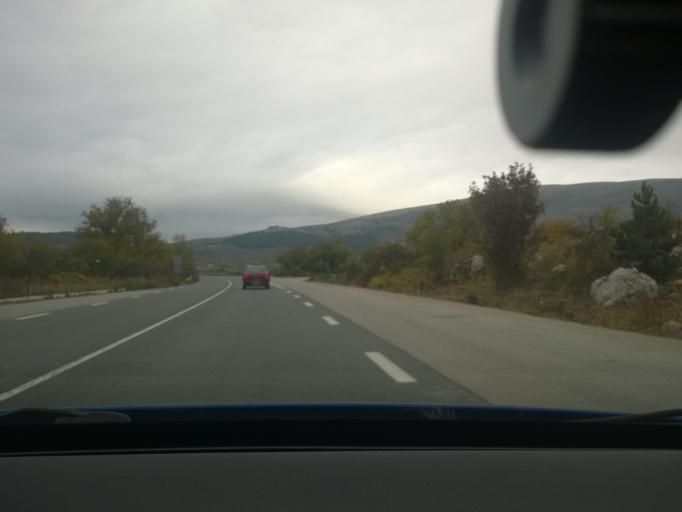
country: BG
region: Sofiya
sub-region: Obshtina Dragoman
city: Dragoman
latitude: 42.9255
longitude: 22.9363
